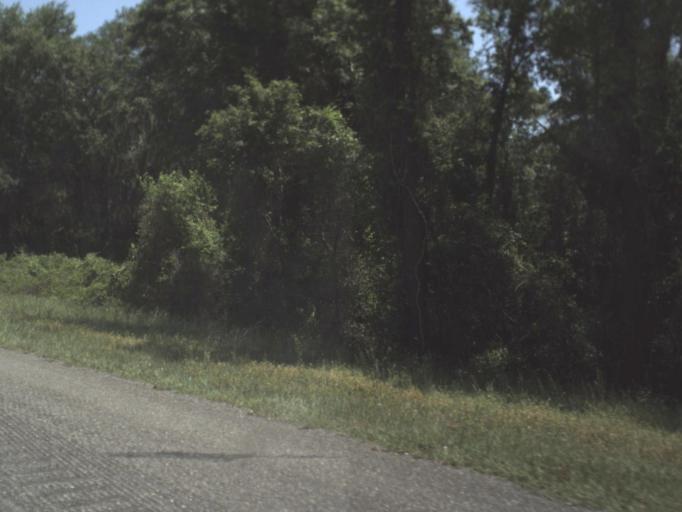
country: US
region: Florida
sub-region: Jefferson County
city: Monticello
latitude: 30.4891
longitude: -83.9858
